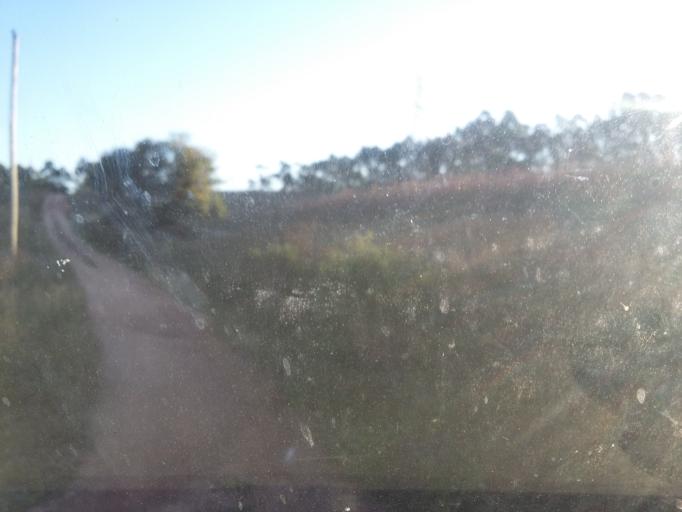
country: BR
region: Rio Grande do Sul
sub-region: Camaqua
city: Camaqua
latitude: -30.7046
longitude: -51.7660
